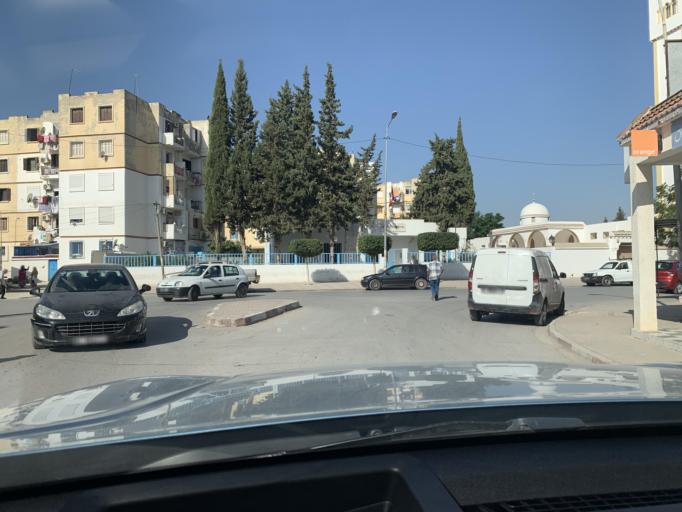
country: TN
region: Manouba
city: Manouba
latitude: 36.8228
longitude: 10.1191
